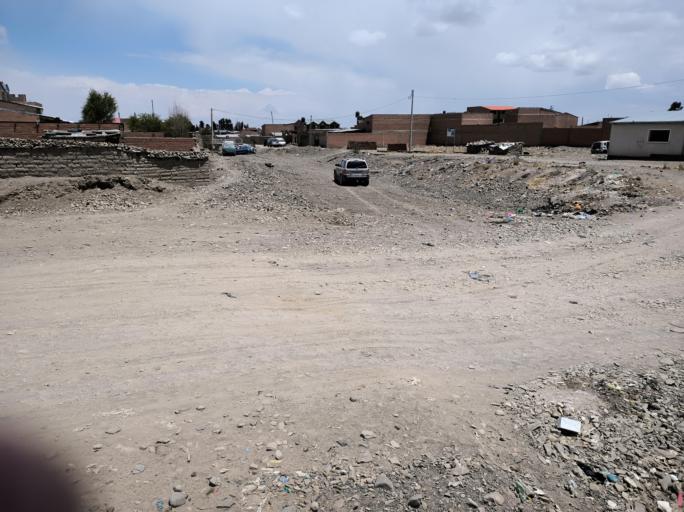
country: BO
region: Oruro
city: Challapata
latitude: -18.8984
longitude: -66.7651
